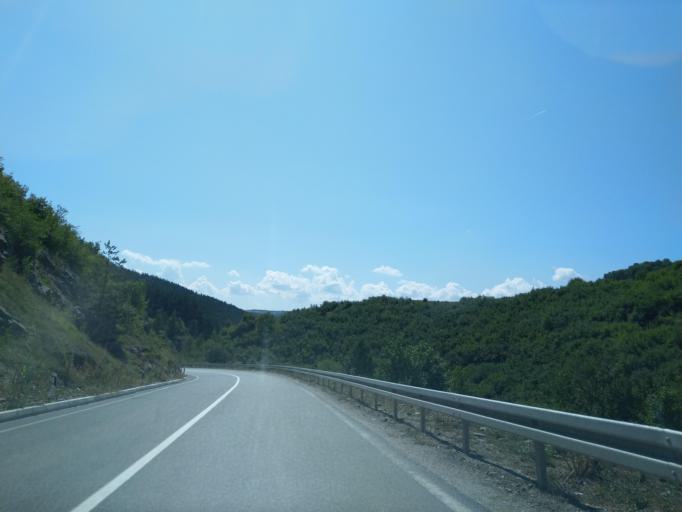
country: RS
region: Central Serbia
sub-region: Zlatiborski Okrug
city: Sjenica
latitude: 43.2960
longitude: 19.9369
